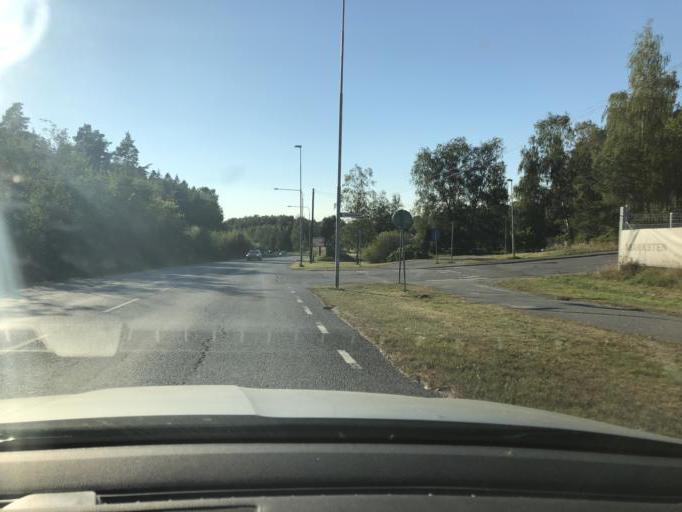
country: SE
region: Stockholm
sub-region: Sodertalje Kommun
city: Soedertaelje
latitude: 59.1834
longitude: 17.5954
